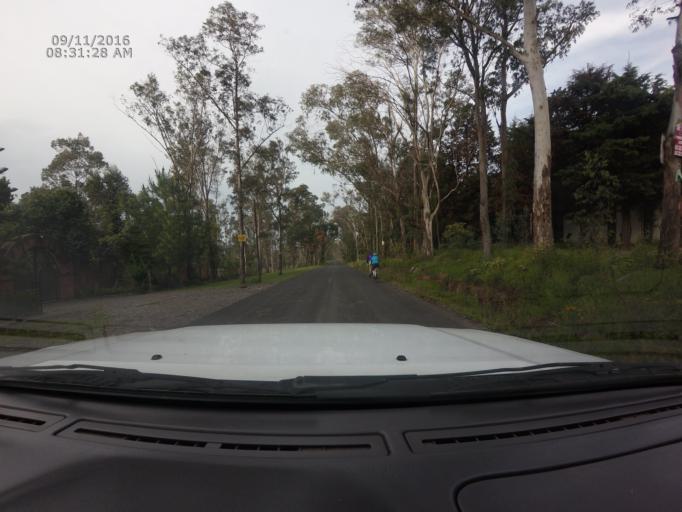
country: MX
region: Michoacan
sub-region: Morelia
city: Morelos
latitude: 19.6324
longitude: -101.2432
